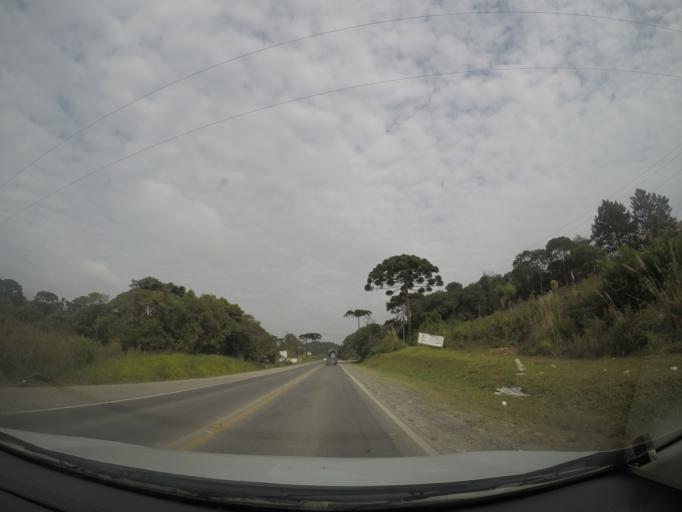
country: BR
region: Parana
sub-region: Almirante Tamandare
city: Almirante Tamandare
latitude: -25.3387
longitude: -49.2582
